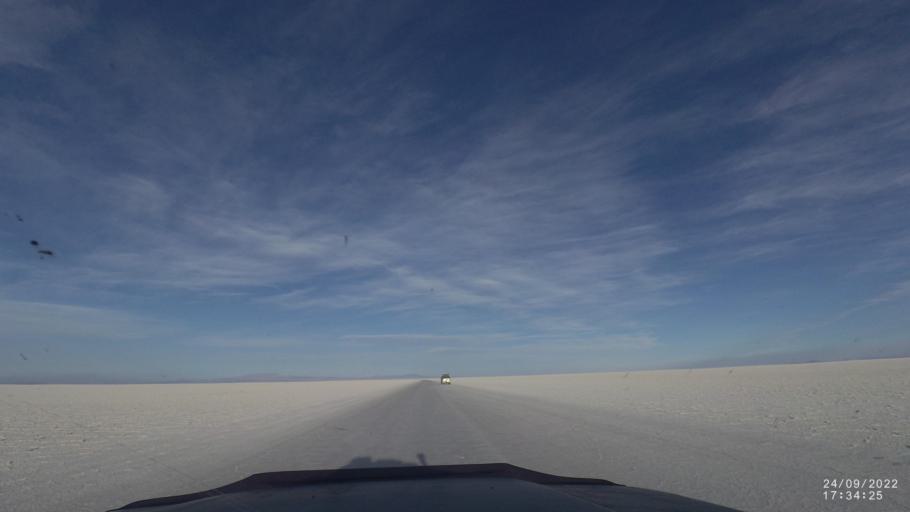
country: BO
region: Potosi
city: Colchani
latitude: -20.3210
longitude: -67.2824
